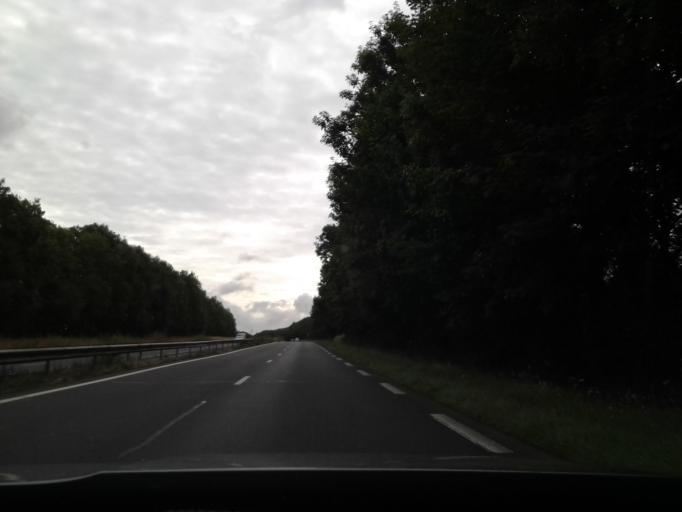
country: FR
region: Lower Normandy
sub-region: Departement du Calvados
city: Isigny-sur-Mer
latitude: 49.3080
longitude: -1.1115
